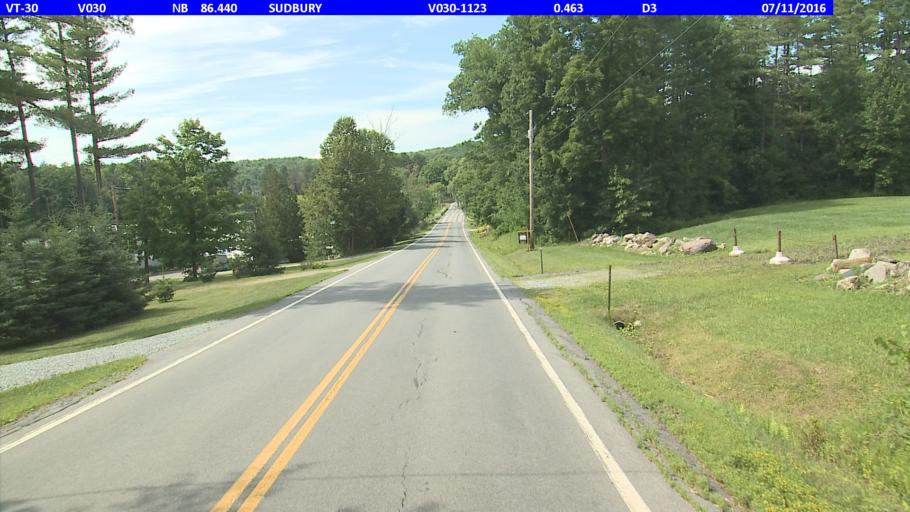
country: US
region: Vermont
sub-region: Rutland County
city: Brandon
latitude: 43.7563
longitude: -73.1929
